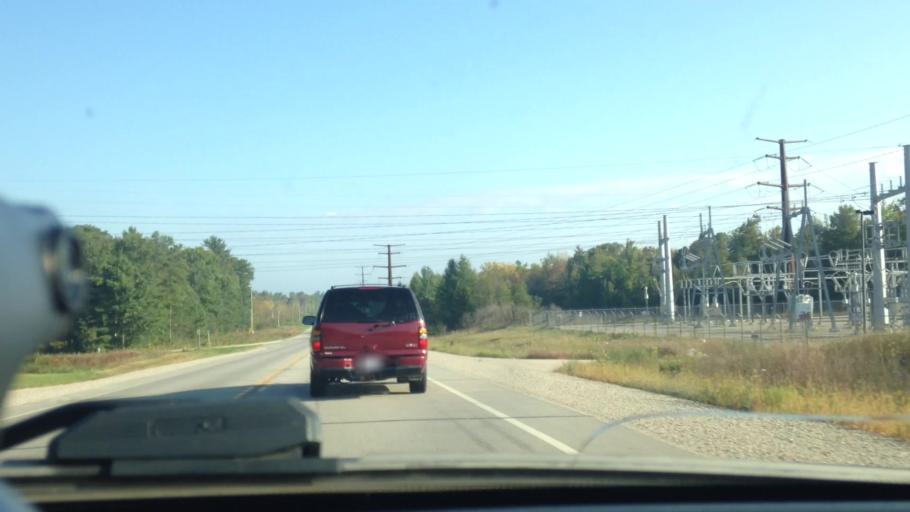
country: US
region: Wisconsin
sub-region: Marinette County
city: Peshtigo
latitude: 45.1759
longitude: -87.9959
